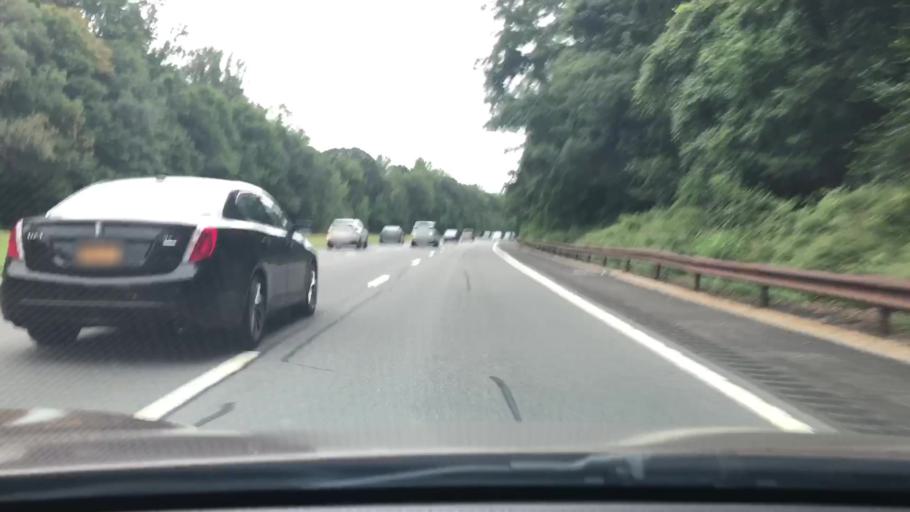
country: US
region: New York
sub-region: Westchester County
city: Ardsley
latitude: 41.0076
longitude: -73.8295
